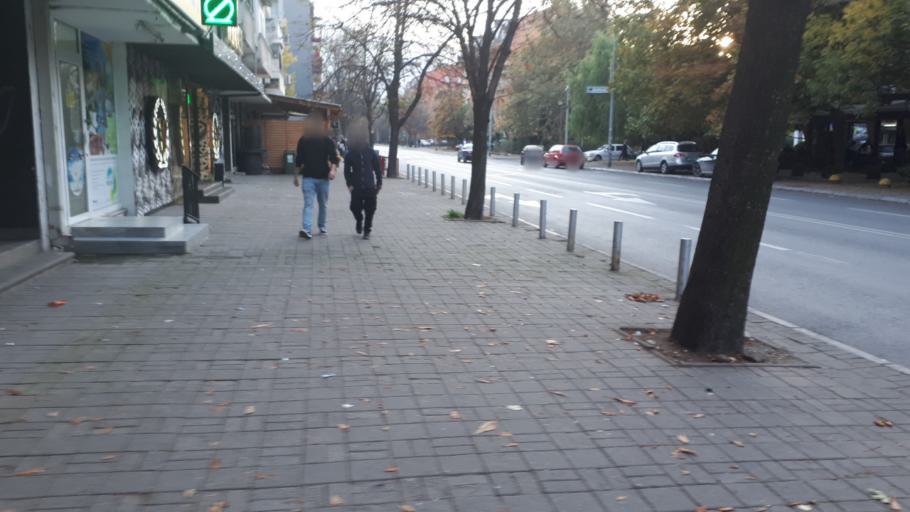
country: MK
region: Karpos
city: Skopje
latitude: 42.0039
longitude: 21.4155
